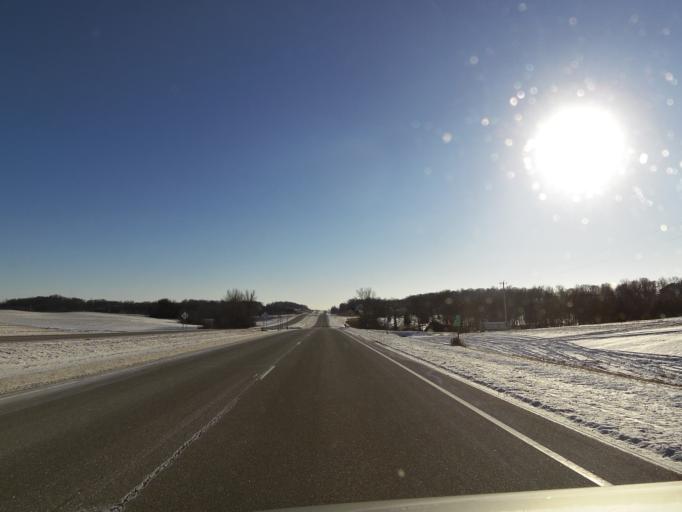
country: US
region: Minnesota
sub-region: Le Sueur County
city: New Prague
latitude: 44.5625
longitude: -93.5018
